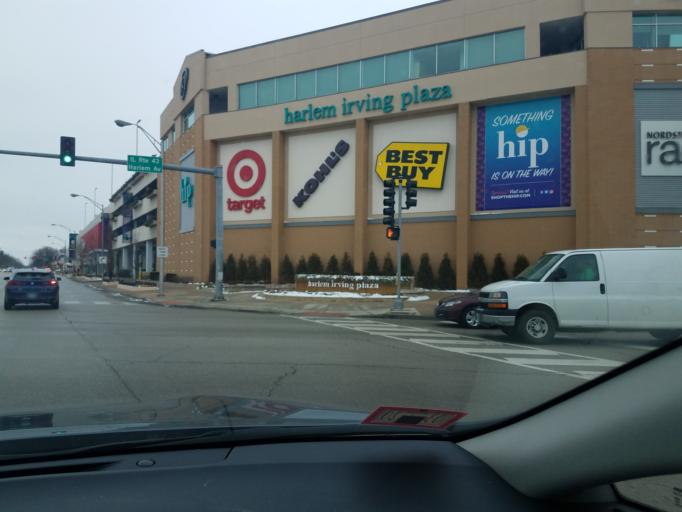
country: US
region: Illinois
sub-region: Cook County
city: Harwood Heights
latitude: 41.9540
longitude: -87.8072
